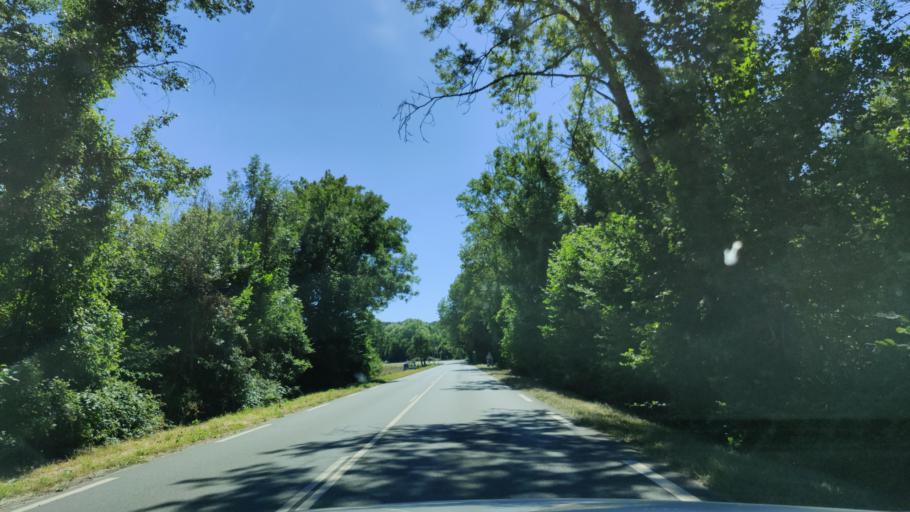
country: FR
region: Ile-de-France
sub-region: Departement de l'Essonne
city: Les Ulis
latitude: 48.6541
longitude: 2.1959
